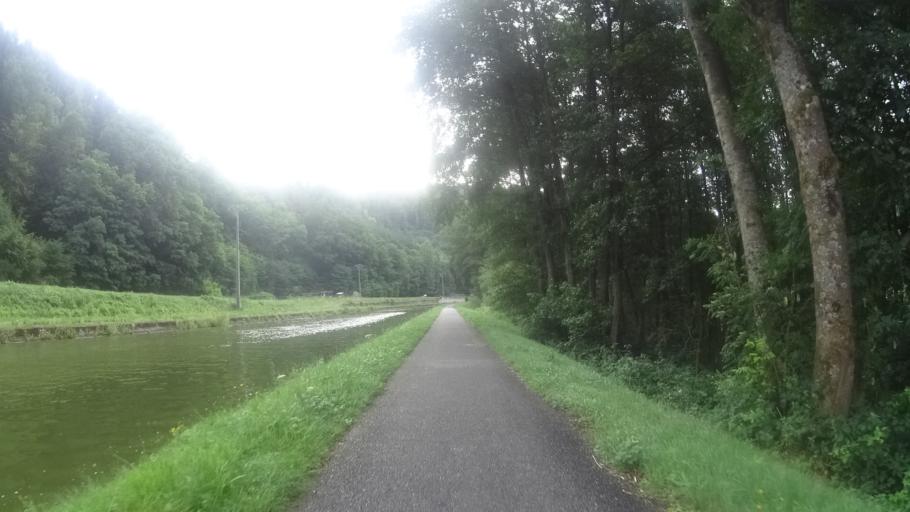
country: FR
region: Lorraine
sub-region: Departement de la Moselle
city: Phalsbourg
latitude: 48.7381
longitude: 7.2685
